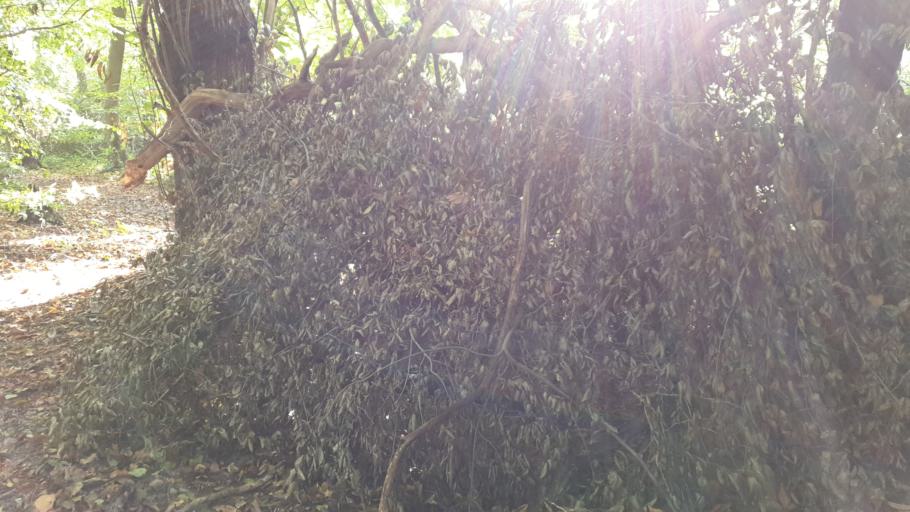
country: FR
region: Haute-Normandie
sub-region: Departement de la Seine-Maritime
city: Saint-Laurent-de-Brevedent
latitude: 49.5296
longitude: 0.2572
